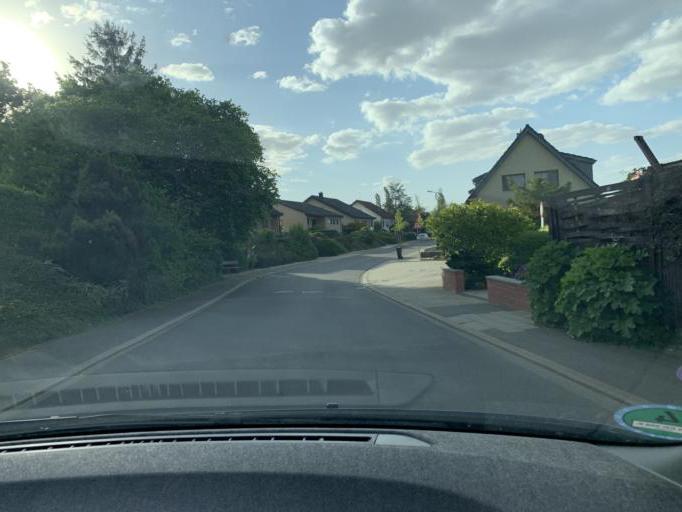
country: DE
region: North Rhine-Westphalia
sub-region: Regierungsbezirk Koln
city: Kreuzau
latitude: 50.7627
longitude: 6.4583
